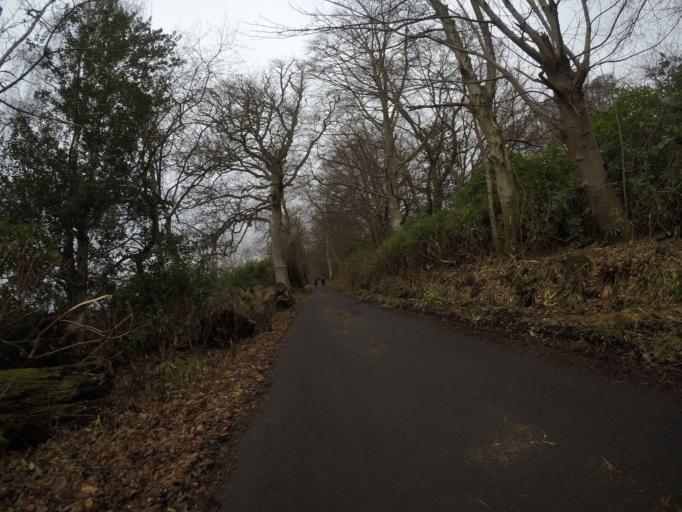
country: GB
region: Scotland
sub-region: North Ayrshire
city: Fairlie
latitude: 55.7635
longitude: -4.8475
